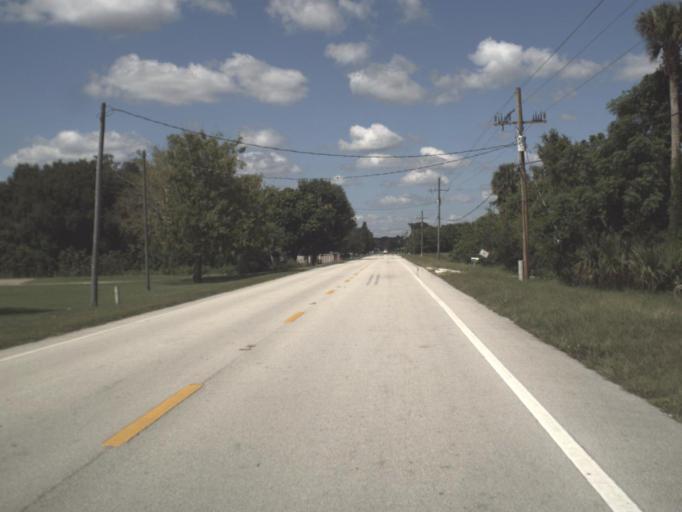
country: US
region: Florida
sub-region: Okeechobee County
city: Taylor Creek
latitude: 27.1428
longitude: -80.6924
